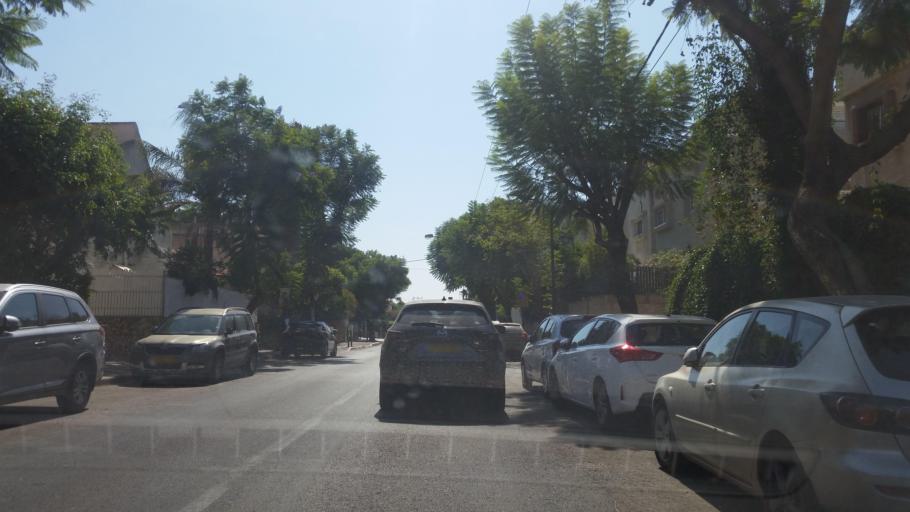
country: IL
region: Central District
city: Ra'anana
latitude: 32.1793
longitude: 34.8847
